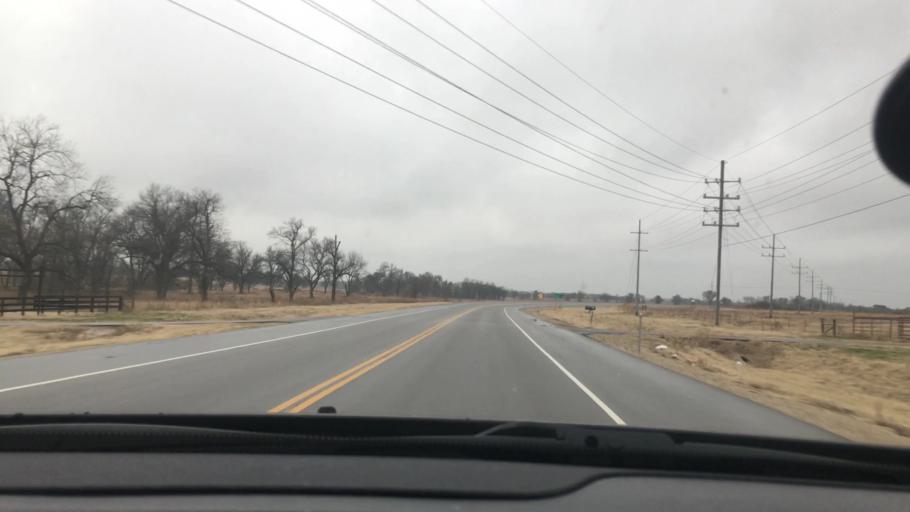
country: US
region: Oklahoma
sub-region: Johnston County
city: Tishomingo
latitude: 34.3503
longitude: -96.6360
